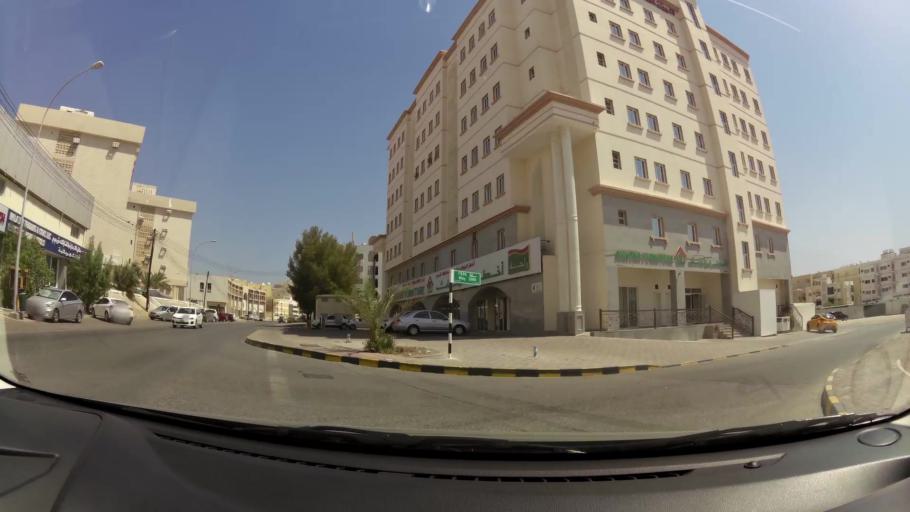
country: OM
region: Muhafazat Masqat
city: Muscat
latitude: 23.5991
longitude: 58.5402
